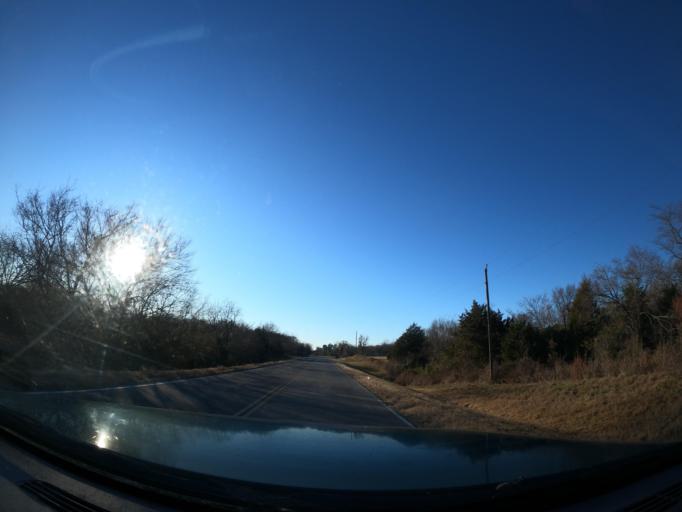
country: US
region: Oklahoma
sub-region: Pittsburg County
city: Hartshorne
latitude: 34.8876
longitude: -95.4753
